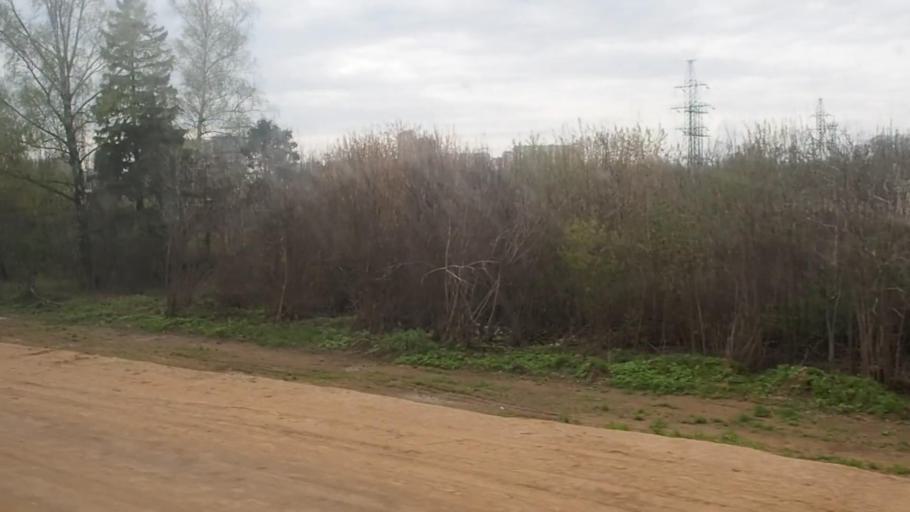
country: RU
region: Moskovskaya
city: Novoivanovskoye
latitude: 55.6892
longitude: 37.3295
